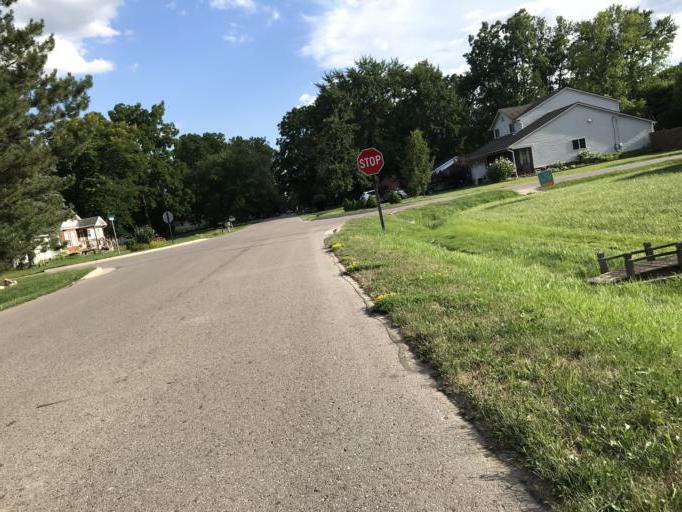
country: US
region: Michigan
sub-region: Oakland County
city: Farmington
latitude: 42.4658
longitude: -83.3486
